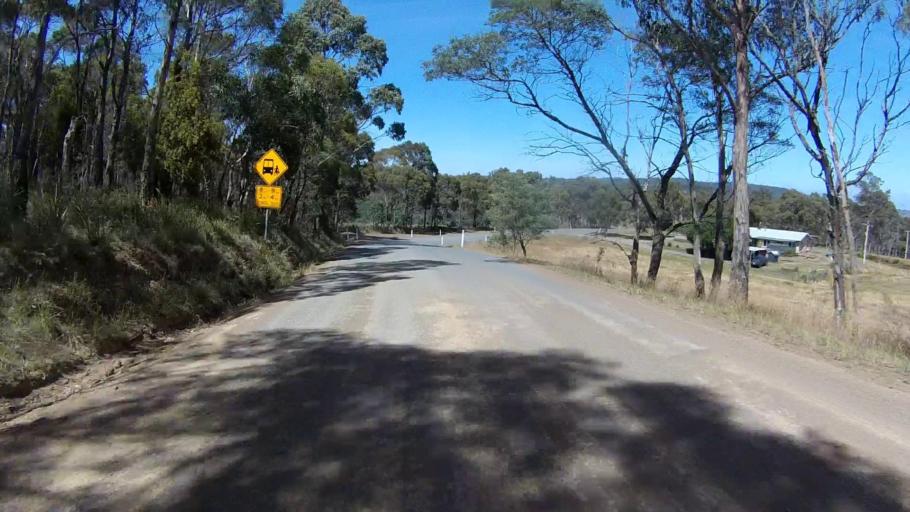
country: AU
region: Tasmania
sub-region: Sorell
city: Sorell
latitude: -42.7462
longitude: 147.7281
